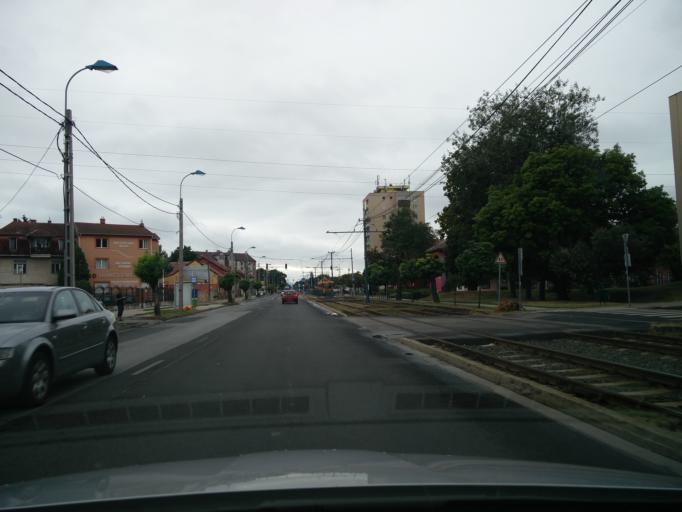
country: HU
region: Budapest
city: Budapest XVIII. keruelet
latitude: 47.4452
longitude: 19.1736
